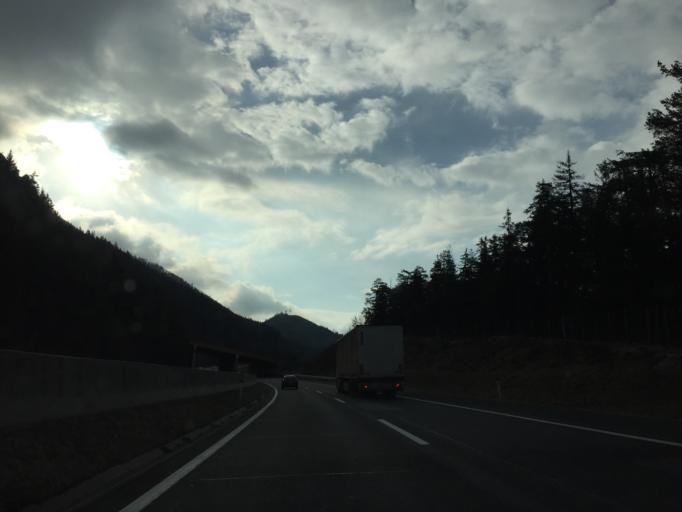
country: AT
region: Salzburg
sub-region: Politischer Bezirk Sankt Johann im Pongau
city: Werfen
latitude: 47.5076
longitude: 13.1736
